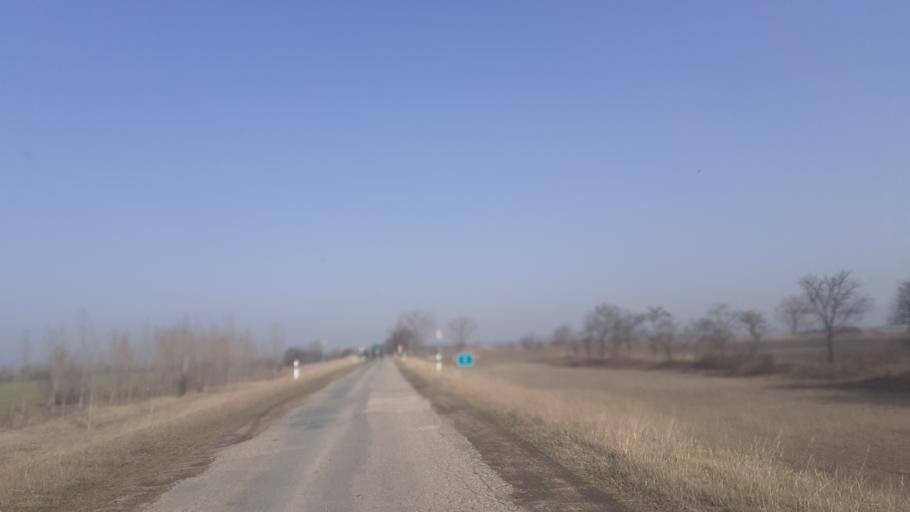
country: HU
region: Bacs-Kiskun
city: Tass
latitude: 47.0467
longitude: 18.9932
